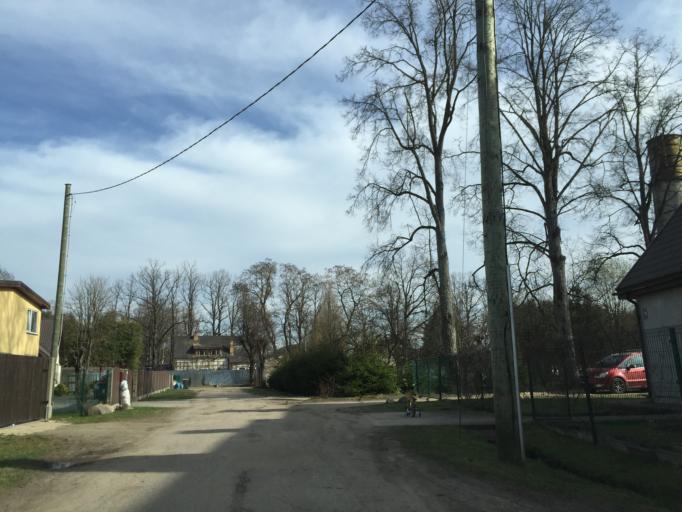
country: LV
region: Ogre
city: Ogre
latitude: 56.8097
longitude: 24.6108
